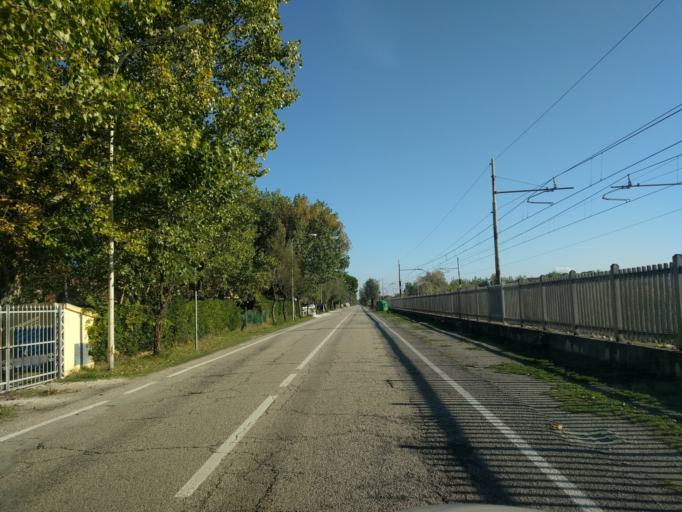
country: IT
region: The Marches
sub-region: Provincia di Pesaro e Urbino
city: Marotta
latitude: 43.7952
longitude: 13.0998
